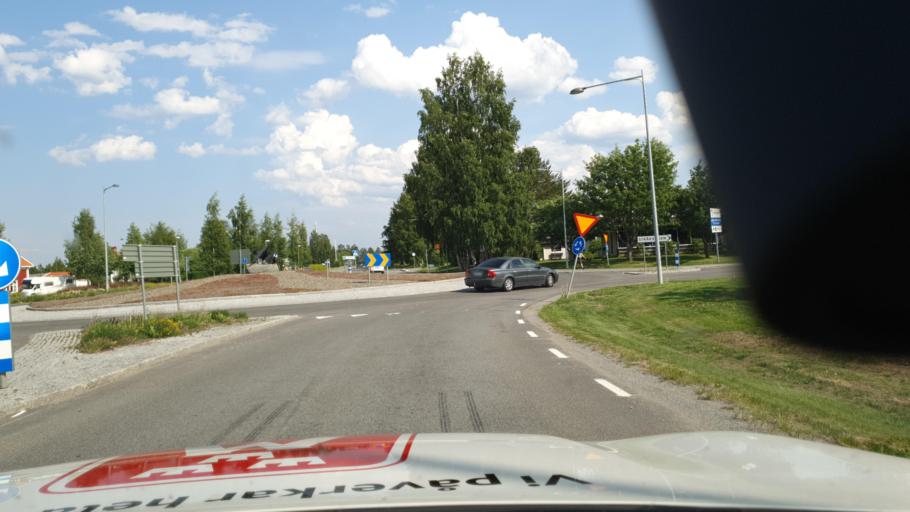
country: SE
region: Vaesterbotten
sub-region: Skelleftea Kommun
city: Viken
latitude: 64.7471
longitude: 20.9124
